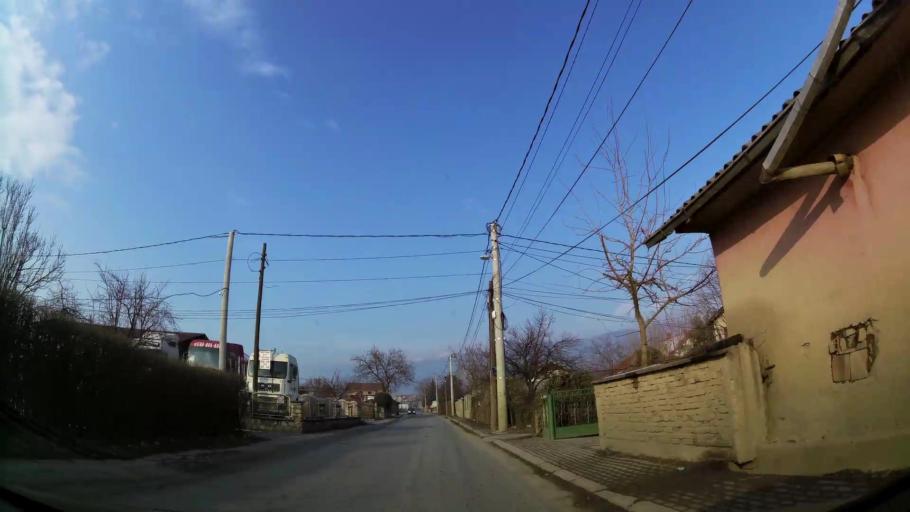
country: MK
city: Creshevo
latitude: 42.0225
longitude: 21.5148
